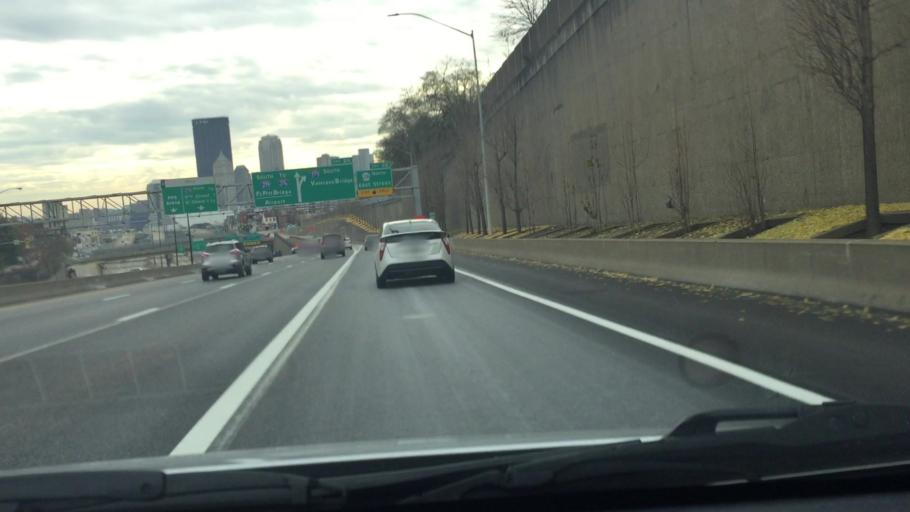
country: US
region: Pennsylvania
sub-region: Allegheny County
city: Pittsburgh
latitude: 40.4616
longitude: -79.9998
